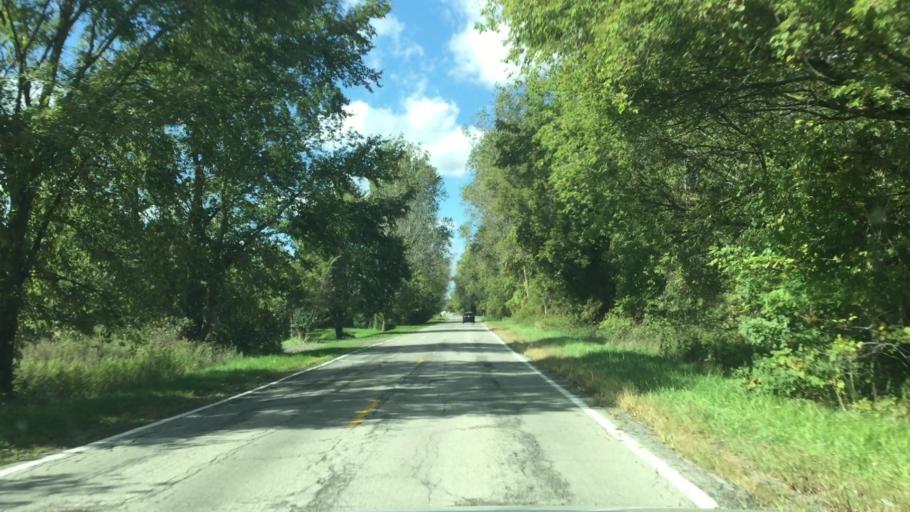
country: US
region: Michigan
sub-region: Genesee County
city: Swartz Creek
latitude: 42.9419
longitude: -83.8480
